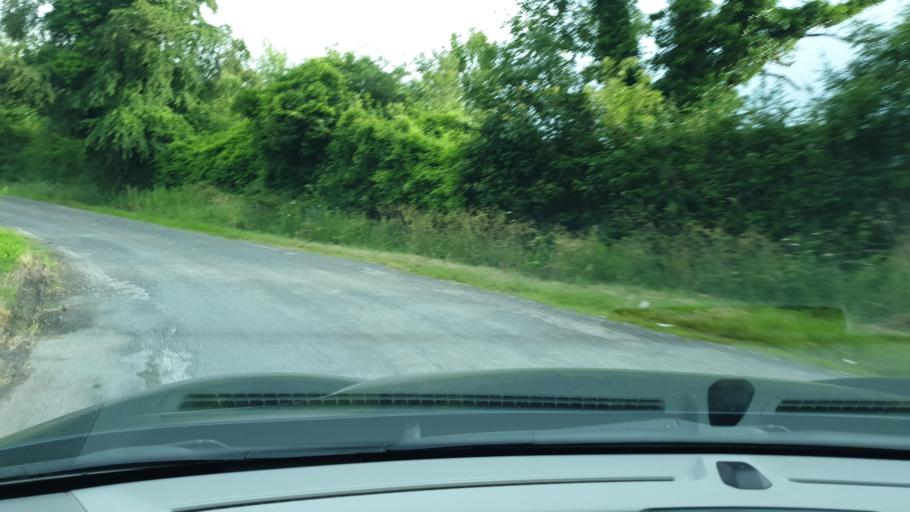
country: IE
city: Confey
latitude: 53.4087
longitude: -6.5120
